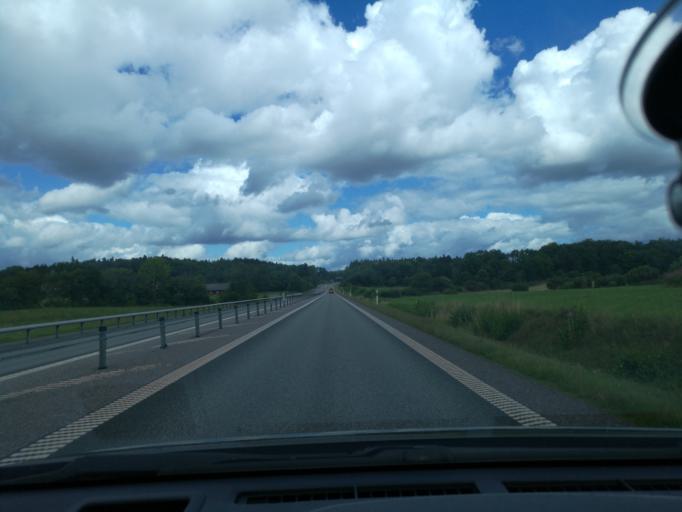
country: SE
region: Skane
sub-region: Hassleholms Kommun
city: Hastveda
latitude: 56.2211
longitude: 13.8813
